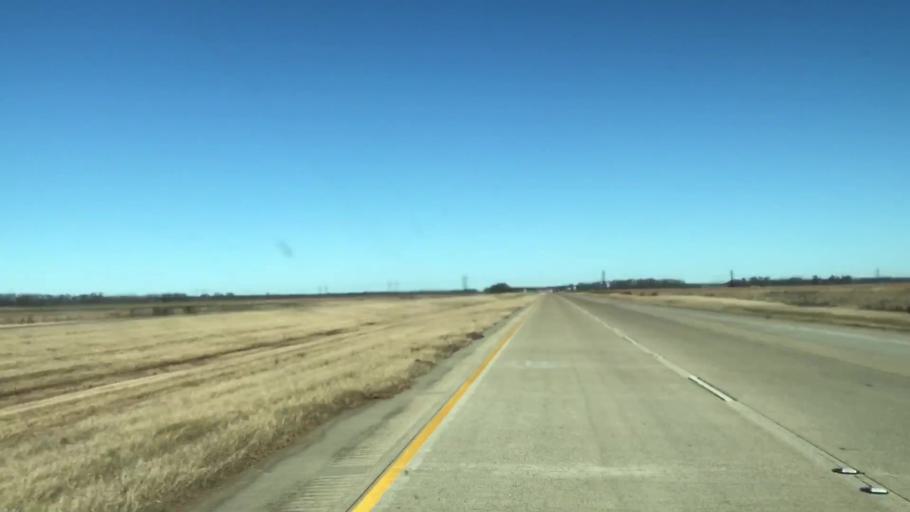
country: US
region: Louisiana
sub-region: Caddo Parish
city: Oil City
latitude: 32.7089
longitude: -93.8641
